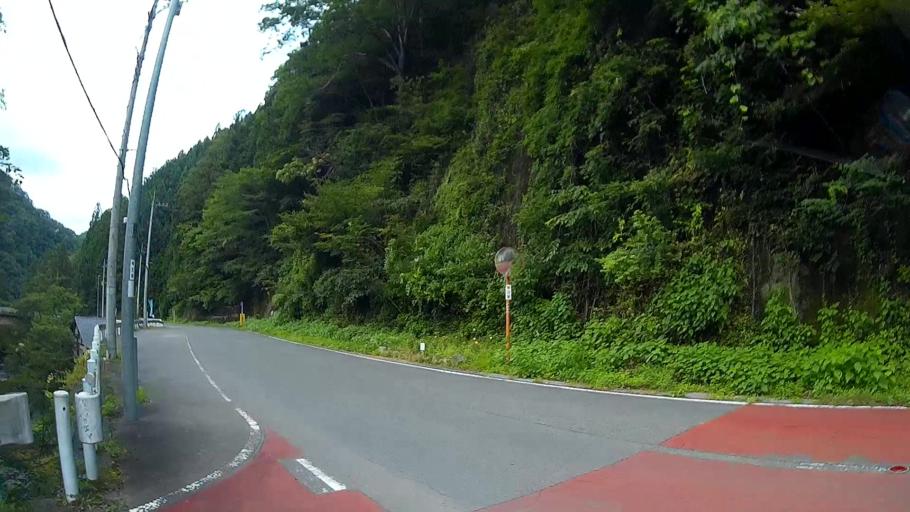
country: JP
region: Saitama
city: Chichibu
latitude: 35.9143
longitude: 139.0804
